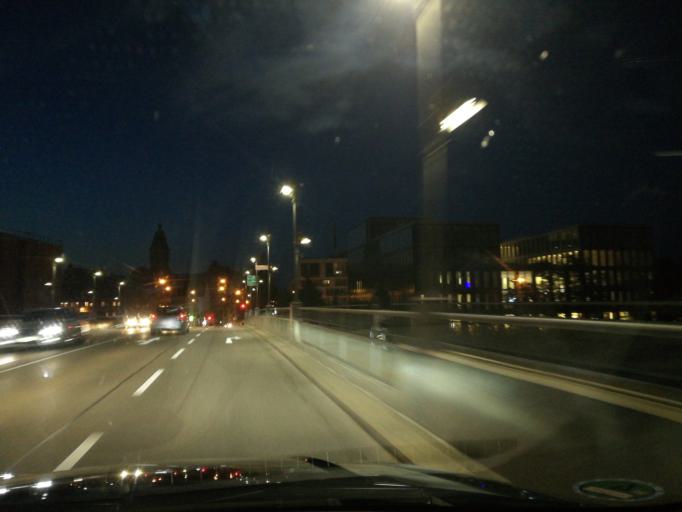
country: DE
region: Bavaria
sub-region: Upper Palatinate
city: Lappersdorf
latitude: 49.0115
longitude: 12.0884
